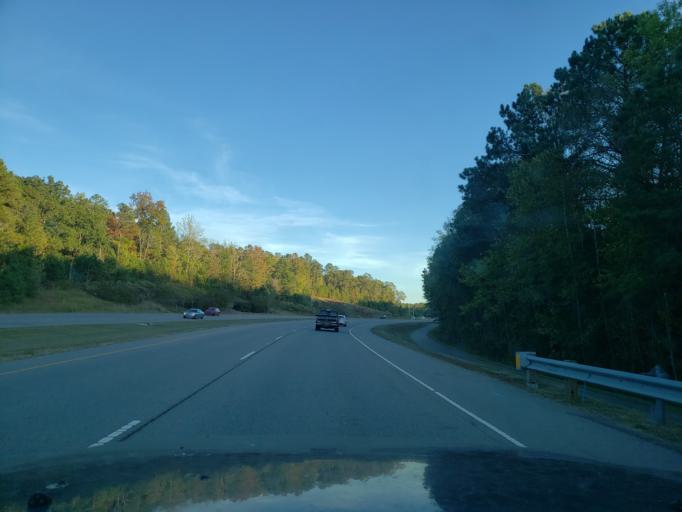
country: US
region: North Carolina
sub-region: Wake County
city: Morrisville
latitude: 35.8499
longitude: -78.8602
